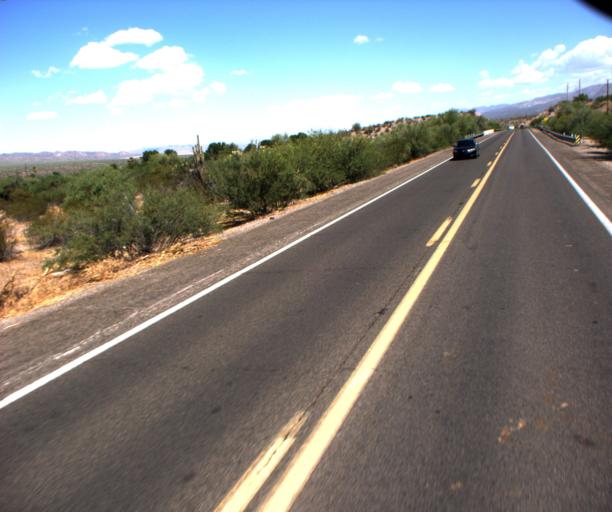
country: US
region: Arizona
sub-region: Pinal County
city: Kearny
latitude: 32.9567
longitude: -110.7475
